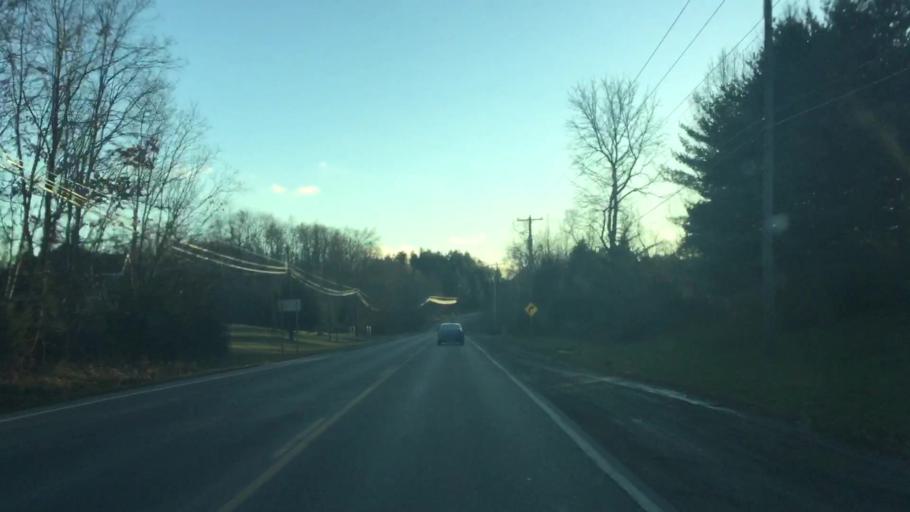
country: US
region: Michigan
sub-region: Genesee County
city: Argentine
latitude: 42.8025
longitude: -83.8215
